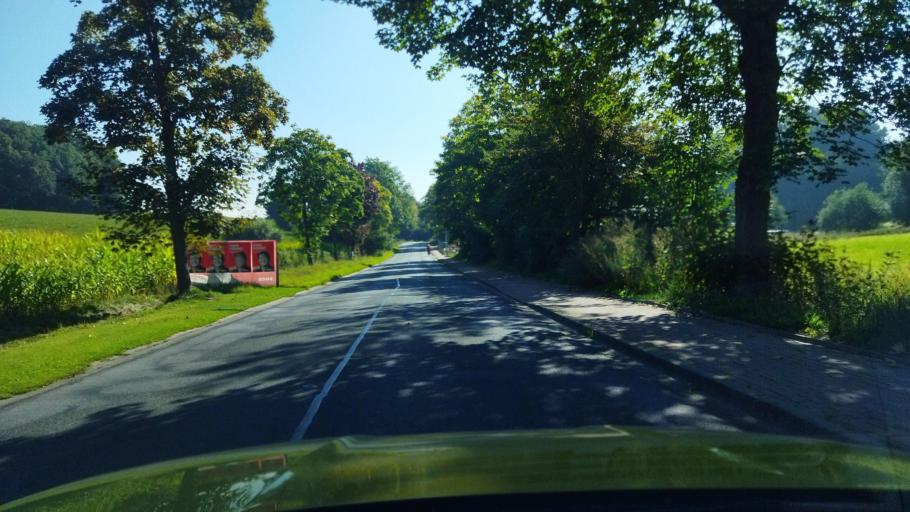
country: DE
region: Lower Saxony
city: Ostercappeln
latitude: 52.3429
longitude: 8.2403
